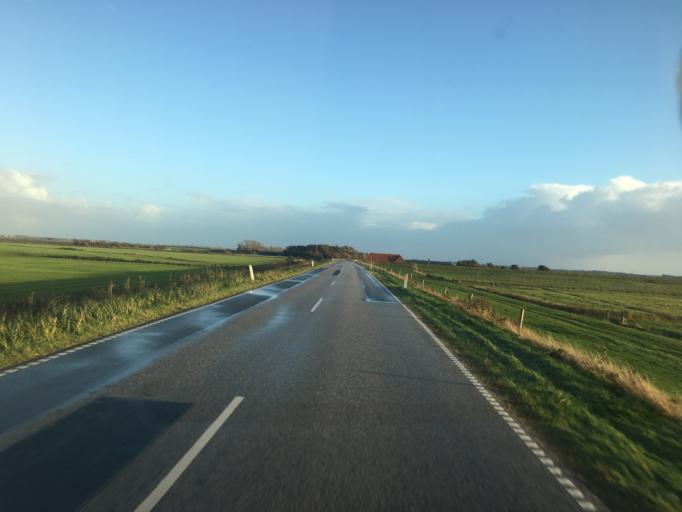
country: DE
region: Schleswig-Holstein
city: Rodenas
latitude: 54.9320
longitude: 8.7180
